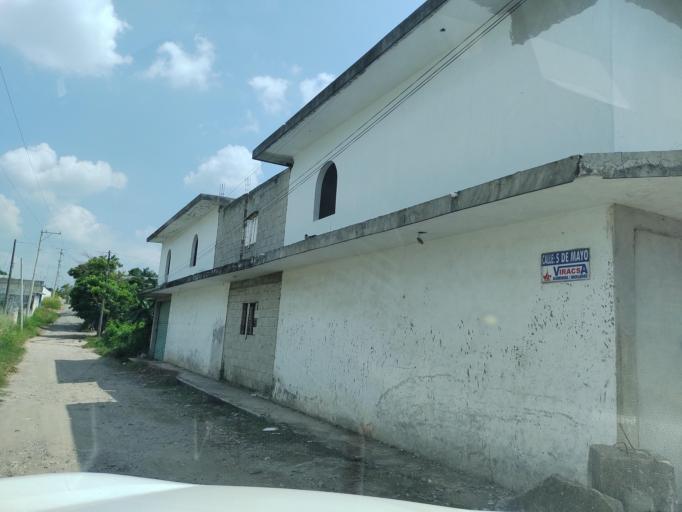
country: MX
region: Veracruz
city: Martinez de la Torre
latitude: 20.0767
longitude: -97.0466
